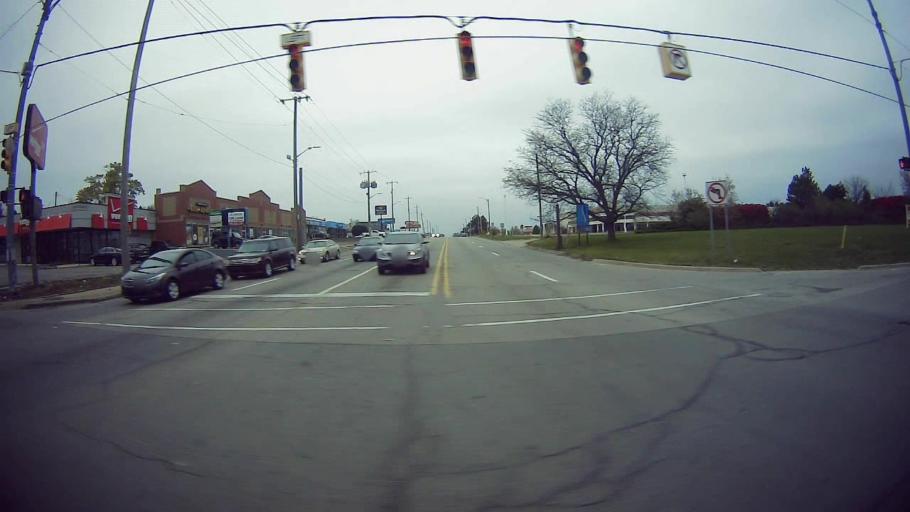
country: US
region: Michigan
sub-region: Oakland County
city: Sylvan Lake
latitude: 42.6400
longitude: -83.3260
